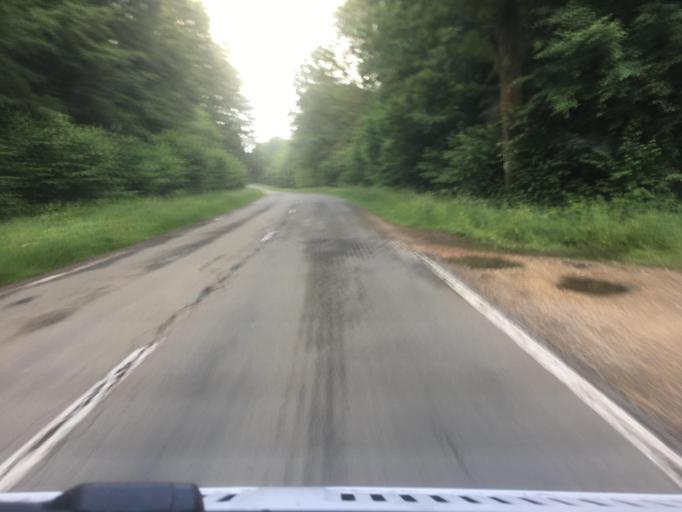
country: BE
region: Wallonia
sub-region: Province du Luxembourg
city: Florenville
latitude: 49.6800
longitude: 5.3349
